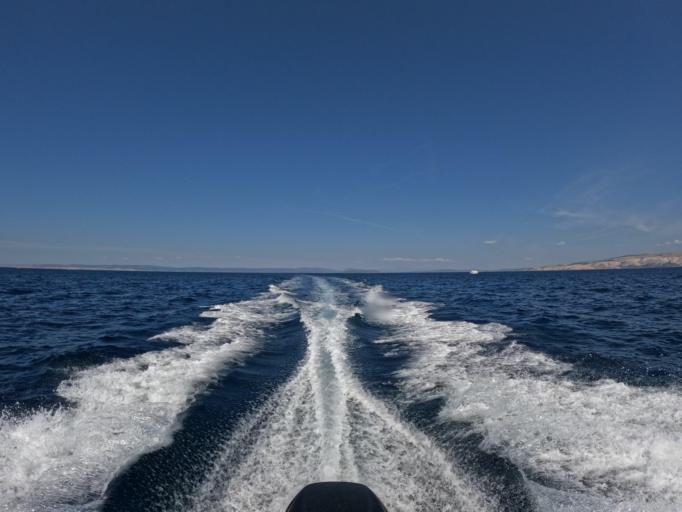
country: HR
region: Primorsko-Goranska
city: Lopar
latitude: 44.8720
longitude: 14.6690
